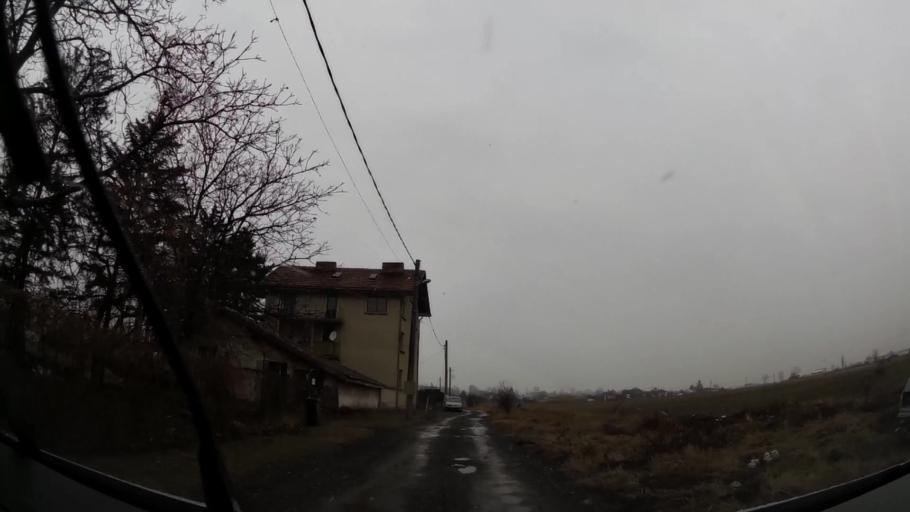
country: BG
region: Sofia-Capital
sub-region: Stolichna Obshtina
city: Sofia
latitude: 42.6663
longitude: 23.4266
